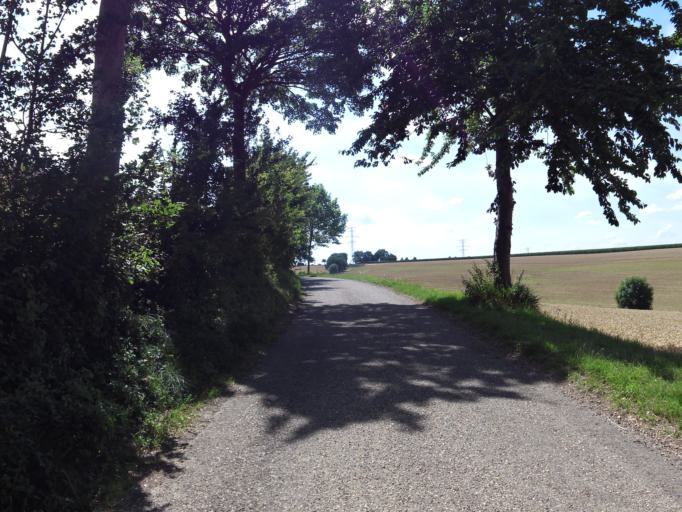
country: NL
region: Limburg
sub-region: Gemeente Voerendaal
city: Kunrade
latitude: 50.8608
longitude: 5.9285
